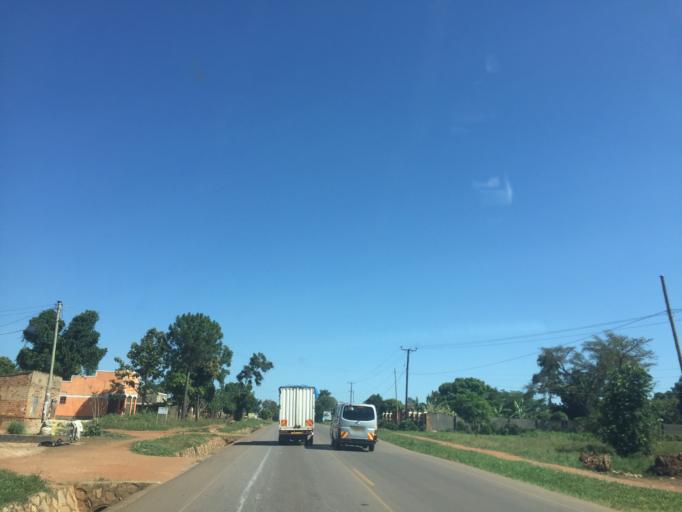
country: UG
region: Central Region
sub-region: Luwero District
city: Luwero
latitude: 0.8107
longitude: 32.5051
